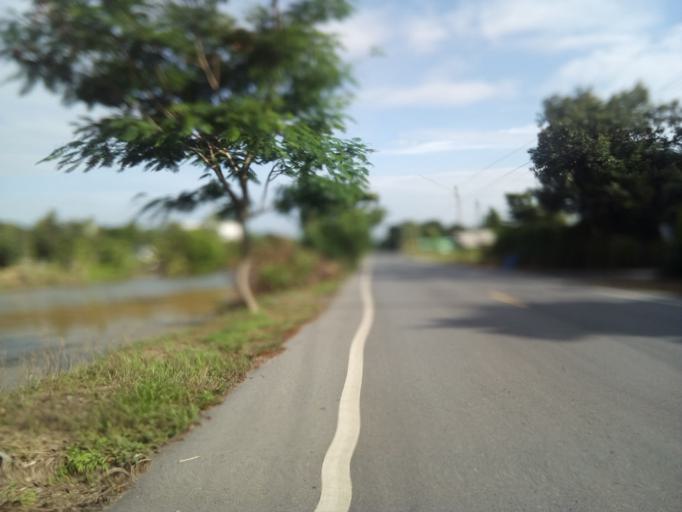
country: TH
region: Pathum Thani
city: Nong Suea
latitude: 14.1011
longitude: 100.8461
